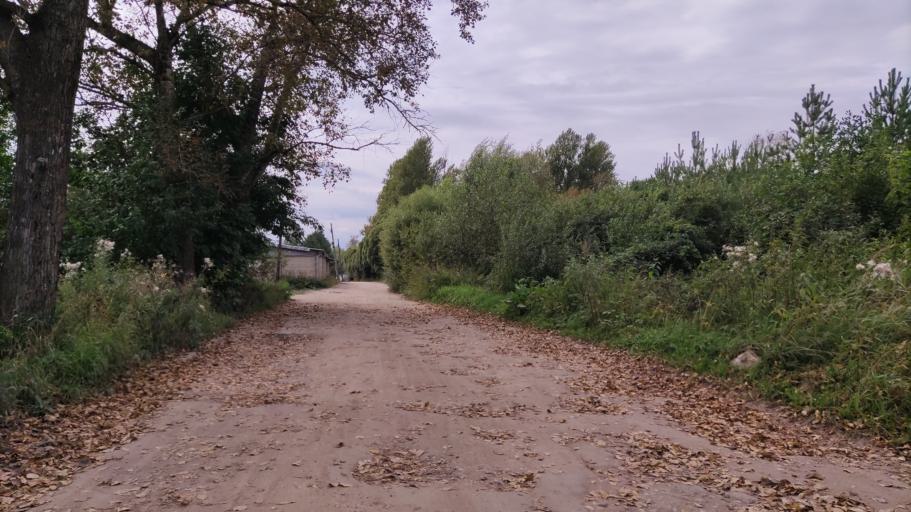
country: RU
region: Tverskaya
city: Rzhev
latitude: 56.2382
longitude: 34.3211
